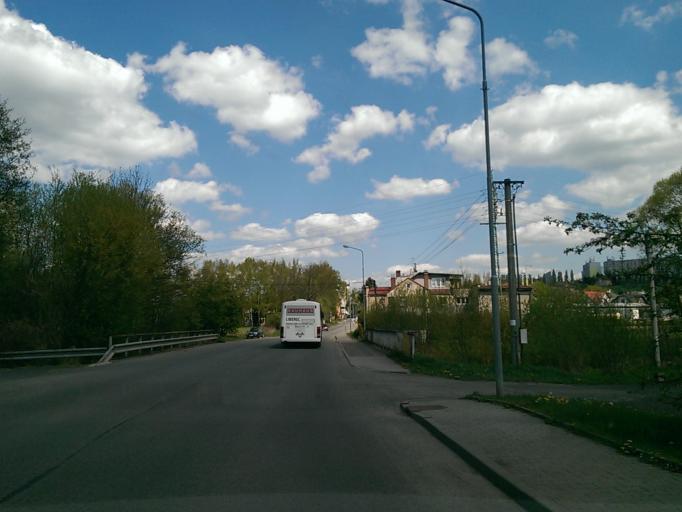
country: CZ
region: Liberecky
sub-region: Okres Semily
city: Turnov
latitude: 50.5774
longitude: 15.1484
